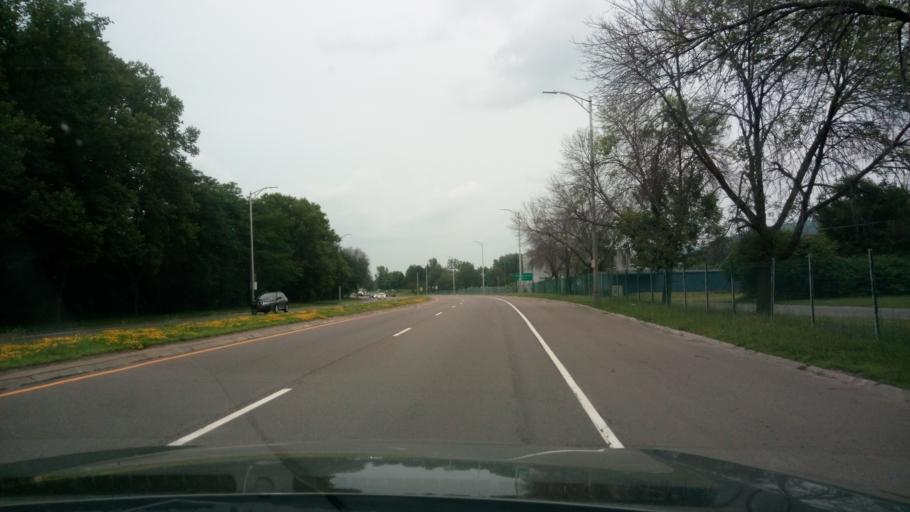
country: US
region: New York
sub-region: Chemung County
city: Elmira
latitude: 42.0980
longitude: -76.8075
